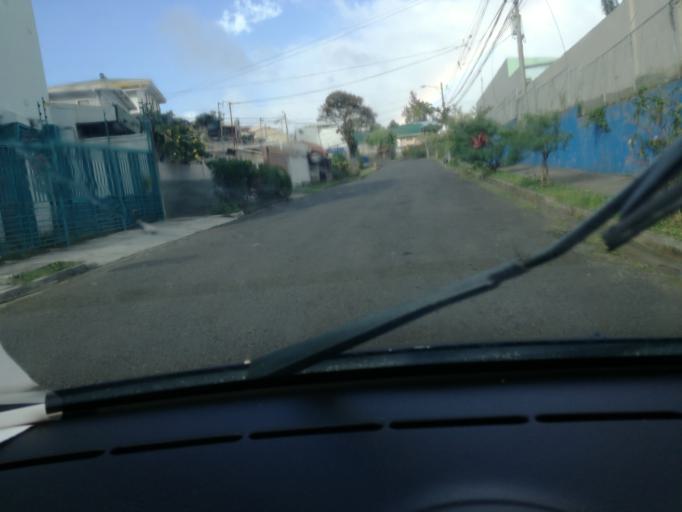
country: CR
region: San Jose
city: San Pedro
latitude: 9.9282
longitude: -84.0512
